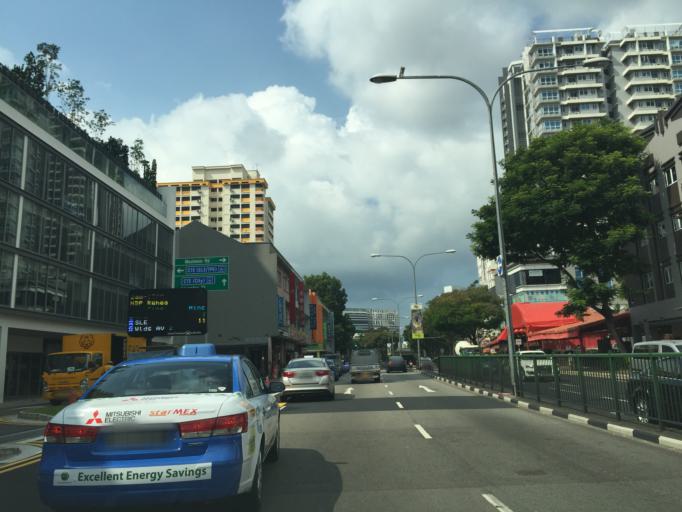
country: SG
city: Singapore
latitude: 1.3223
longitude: 103.8528
